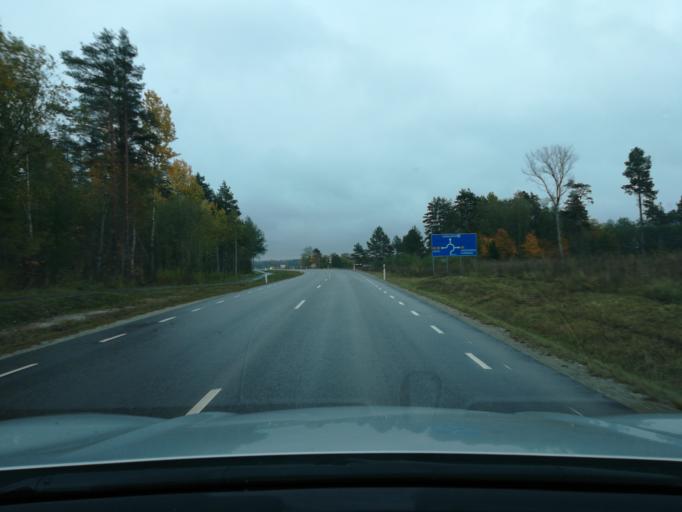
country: EE
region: Ida-Virumaa
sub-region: Johvi vald
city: Johvi
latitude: 59.2955
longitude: 27.4892
